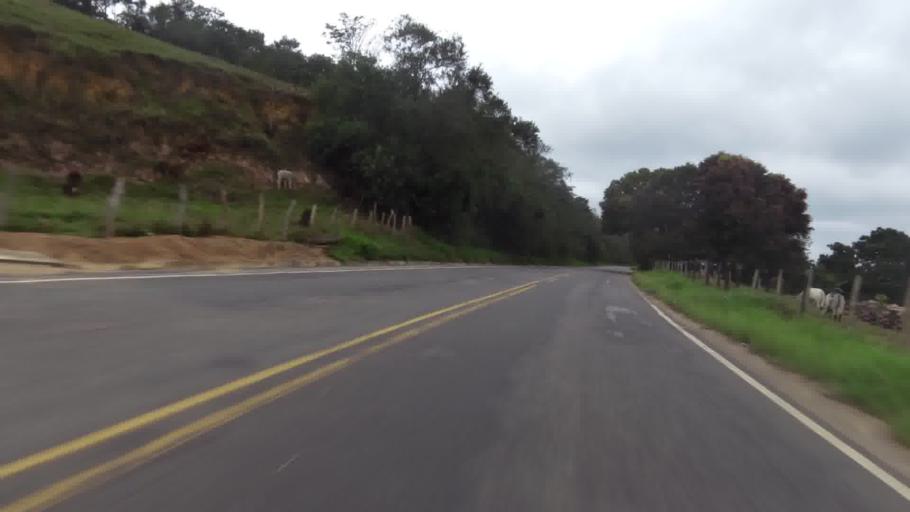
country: BR
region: Espirito Santo
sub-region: Alfredo Chaves
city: Alfredo Chaves
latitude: -20.6833
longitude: -40.7062
